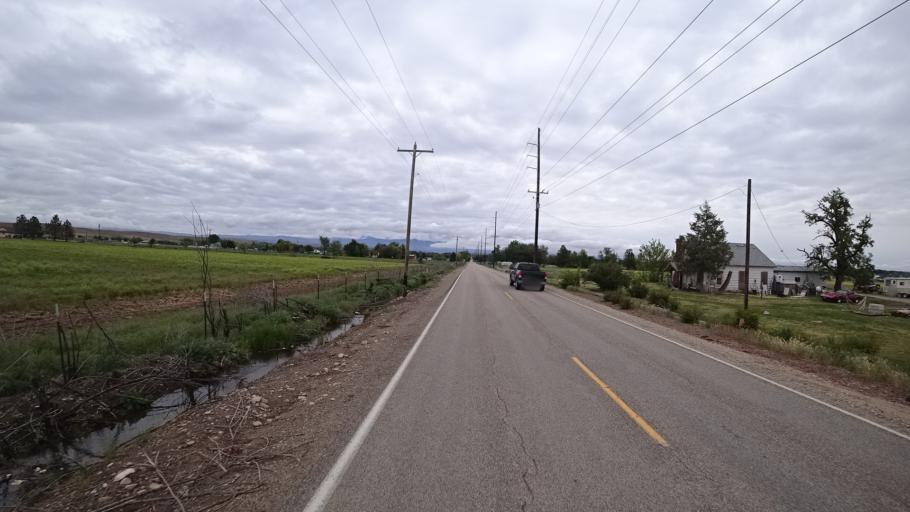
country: US
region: Idaho
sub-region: Ada County
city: Star
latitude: 43.7210
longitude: -116.4275
